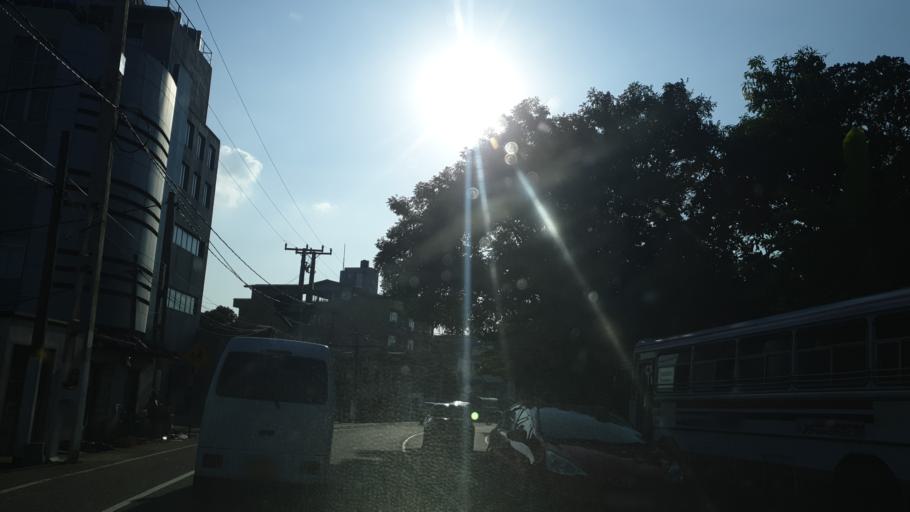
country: LK
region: Western
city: Galkissa
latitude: 6.8543
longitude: 79.8868
